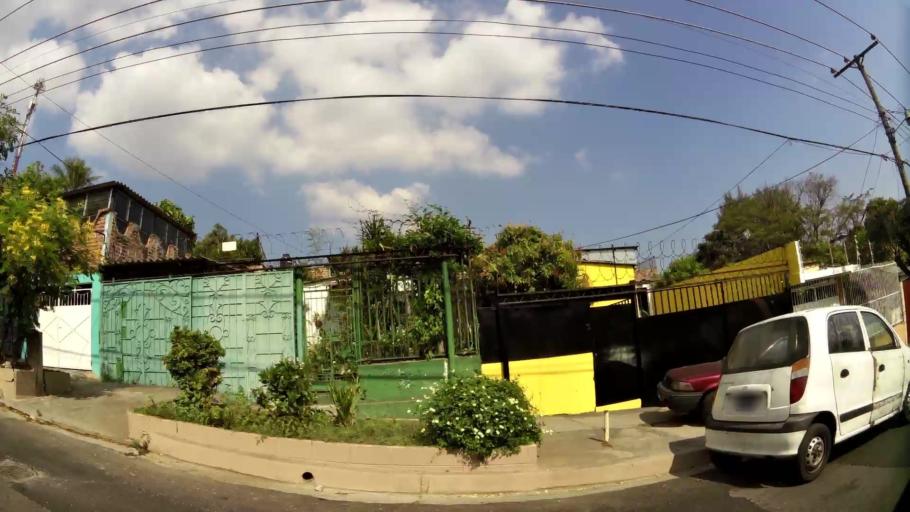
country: SV
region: San Salvador
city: Delgado
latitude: 13.7104
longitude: -89.1681
